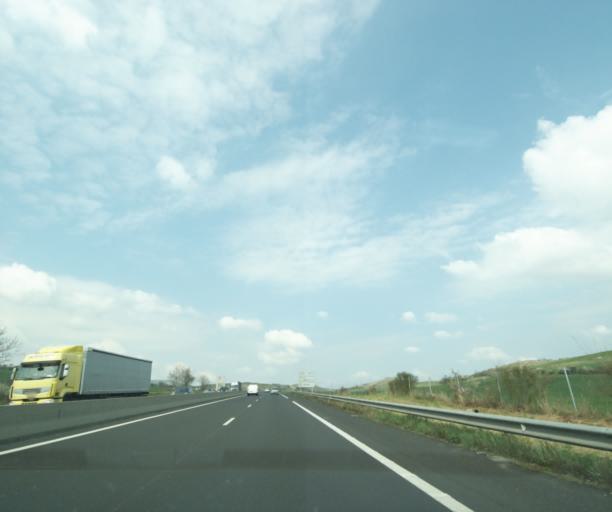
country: FR
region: Auvergne
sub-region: Departement du Puy-de-Dome
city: Tallende
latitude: 45.6768
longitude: 3.1425
